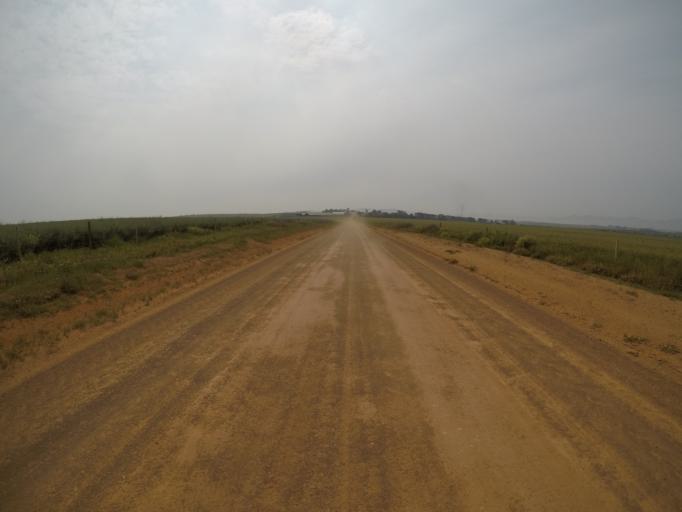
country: ZA
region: Western Cape
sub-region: City of Cape Town
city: Kraaifontein
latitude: -33.7116
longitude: 18.6865
